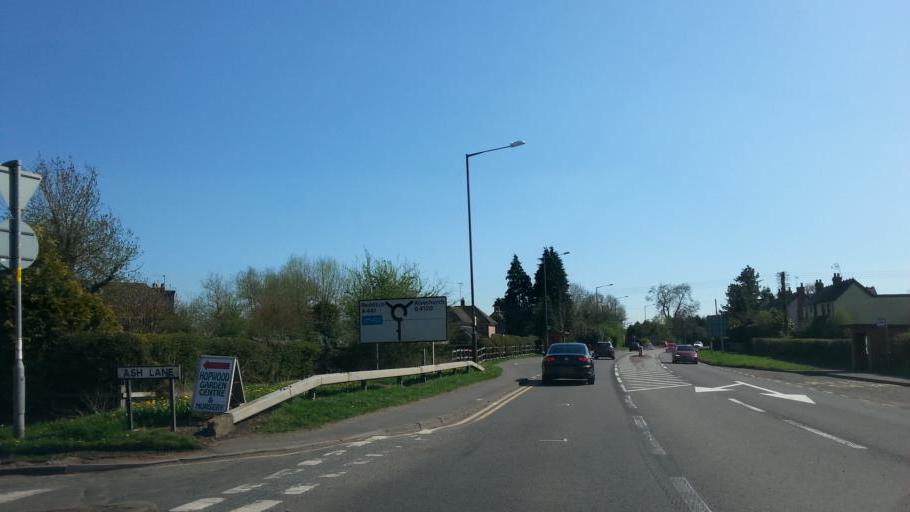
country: GB
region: England
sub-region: Worcestershire
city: Alvechurch
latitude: 52.3712
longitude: -1.9556
